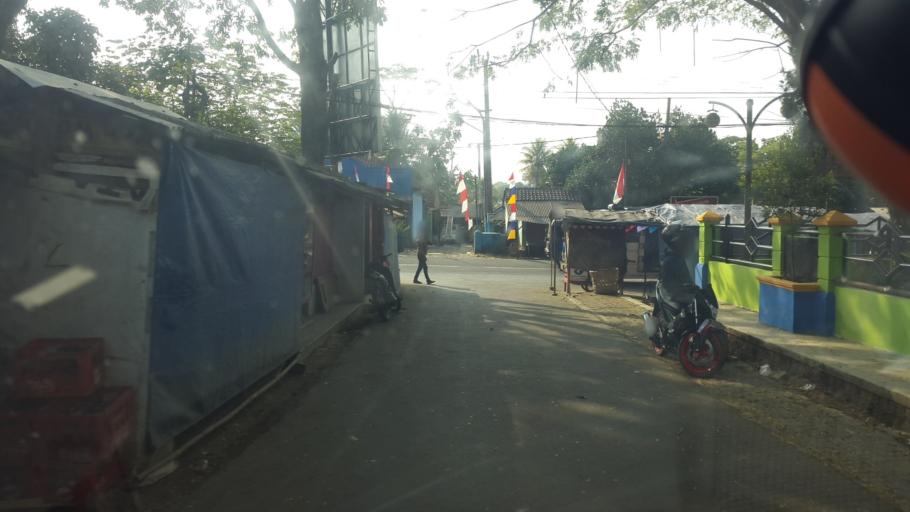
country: ID
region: West Java
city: Jampang Kulon
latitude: -7.2595
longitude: 106.6256
